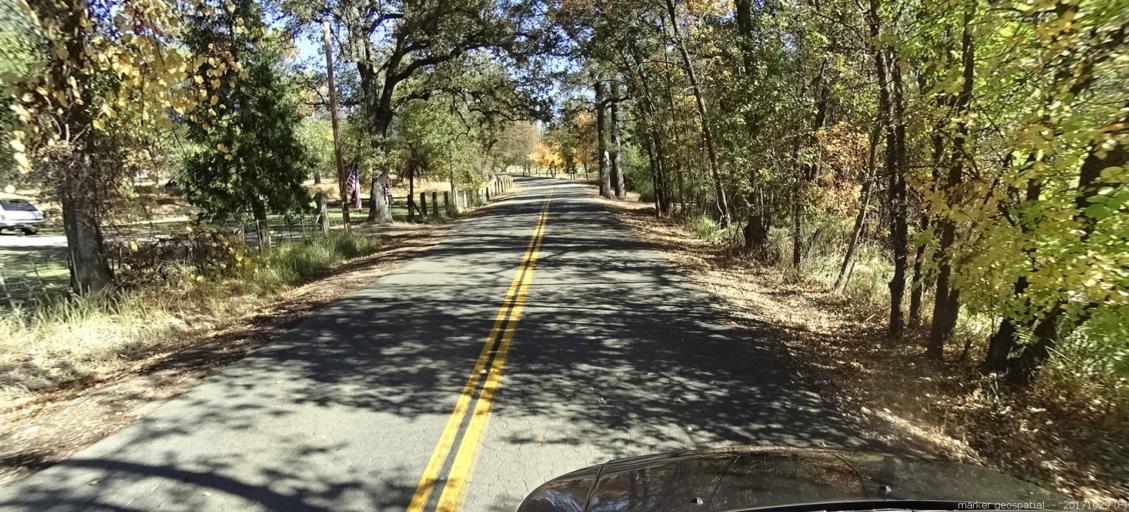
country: US
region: California
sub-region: Shasta County
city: Shasta
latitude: 40.4825
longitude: -122.6608
